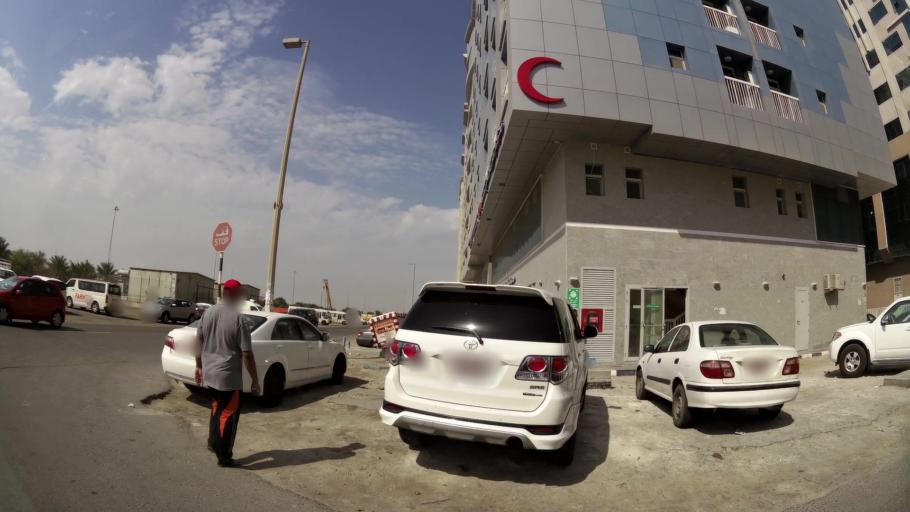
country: AE
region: Abu Dhabi
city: Abu Dhabi
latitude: 24.3432
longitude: 54.5300
